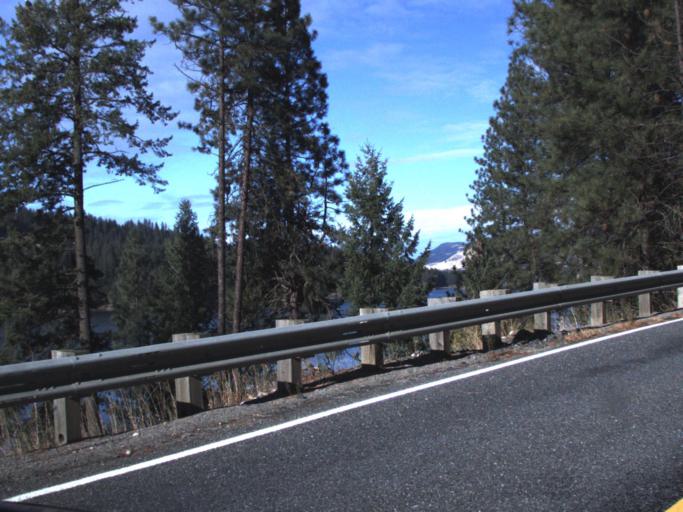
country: US
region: Washington
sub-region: Stevens County
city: Kettle Falls
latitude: 48.2350
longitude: -118.1513
